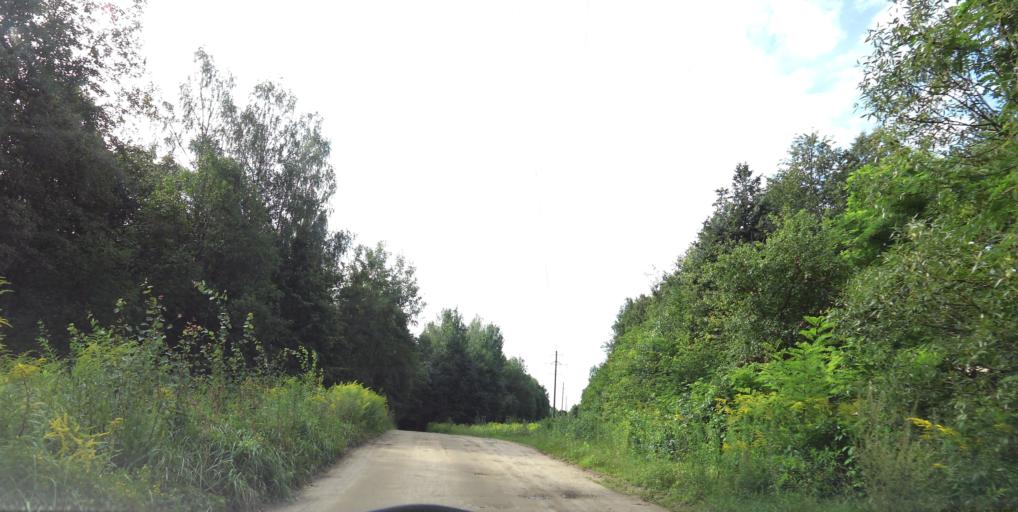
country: LT
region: Vilnius County
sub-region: Vilnius
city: Fabijoniskes
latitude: 54.7390
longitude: 25.2831
